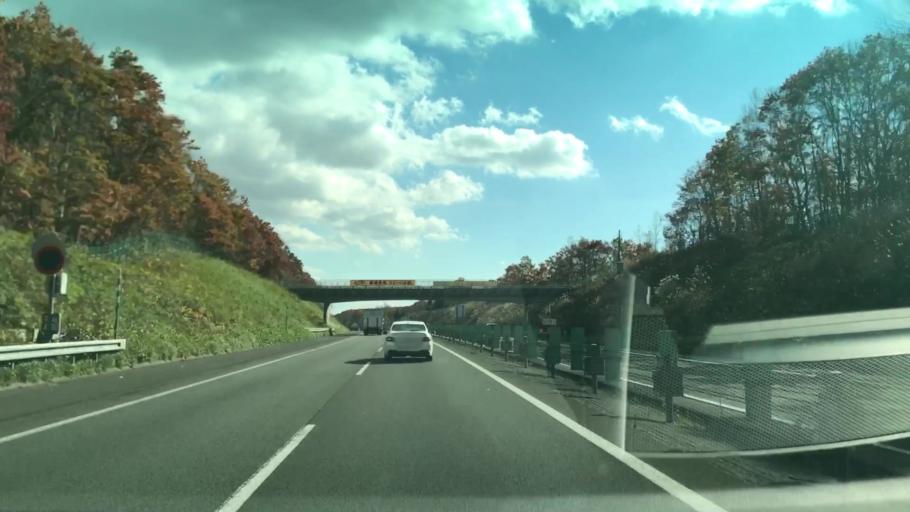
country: JP
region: Hokkaido
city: Kitahiroshima
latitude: 42.9380
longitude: 141.5236
